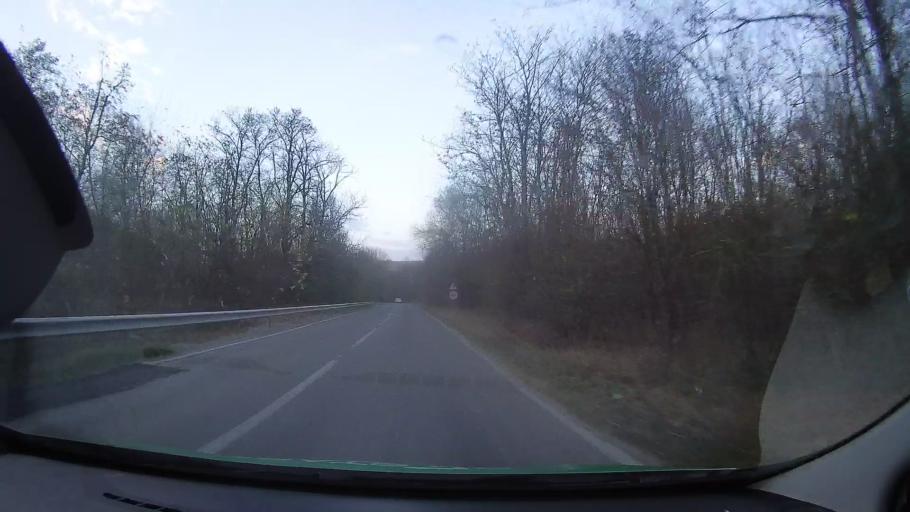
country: RO
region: Constanta
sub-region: Comuna Baneasa
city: Baneasa
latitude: 44.0846
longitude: 27.6668
